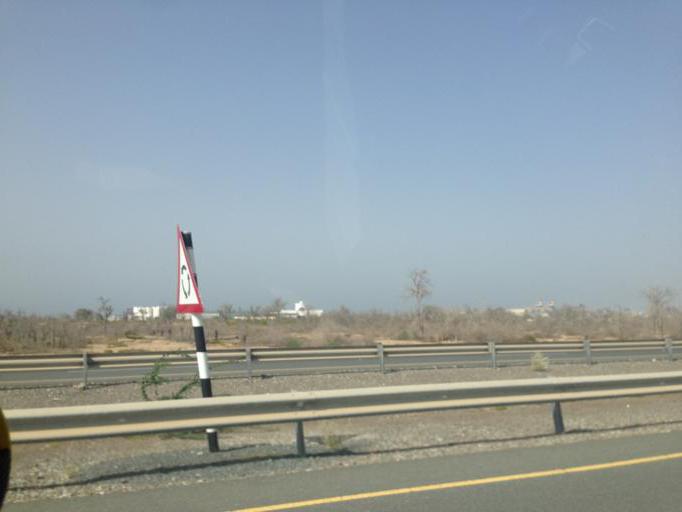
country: OM
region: Al Batinah
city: Barka'
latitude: 23.6983
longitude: 57.9580
